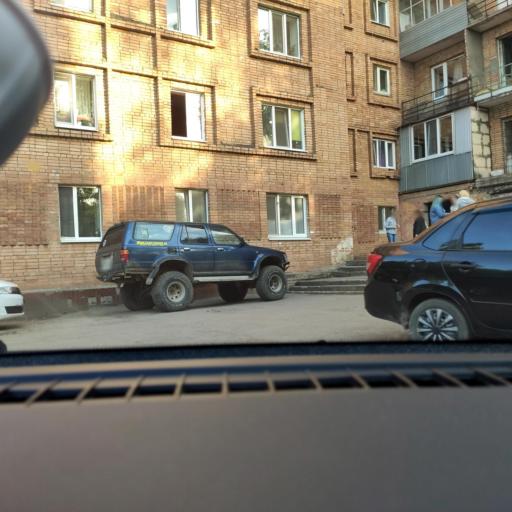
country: RU
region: Samara
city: Smyshlyayevka
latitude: 53.2169
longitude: 50.2844
